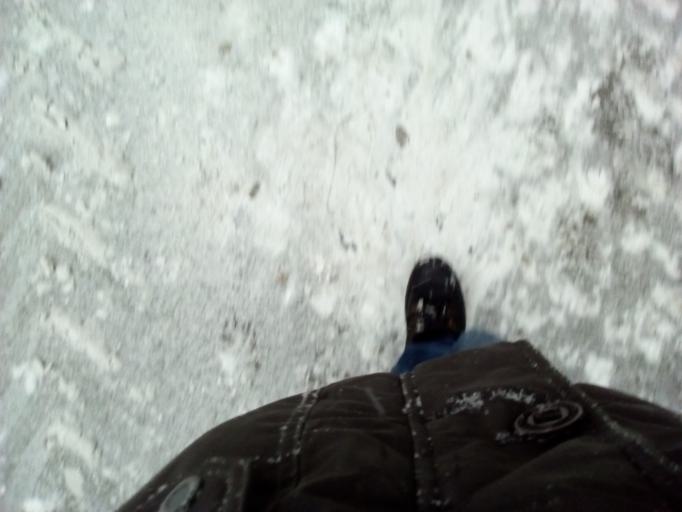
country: RU
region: Moscow
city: Tsaritsyno
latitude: 55.6345
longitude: 37.6697
